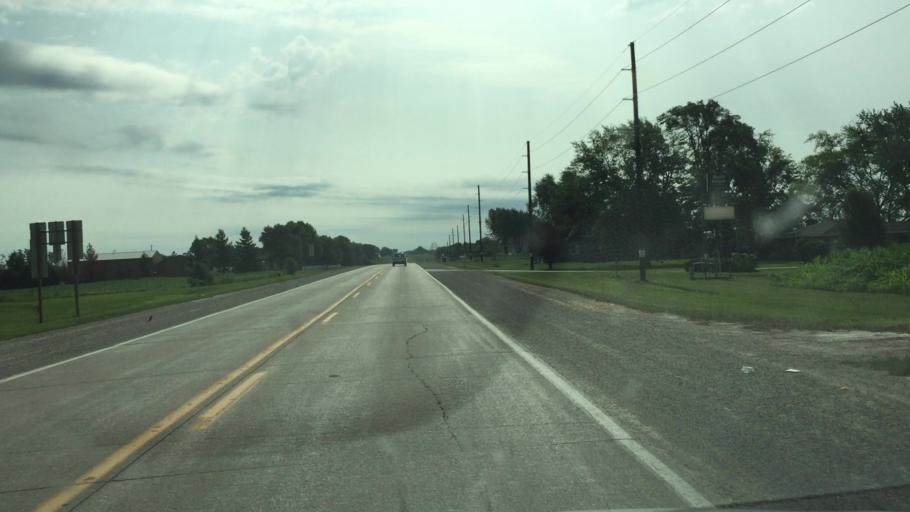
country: US
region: Illinois
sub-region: Hancock County
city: Nauvoo
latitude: 40.6390
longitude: -91.5525
